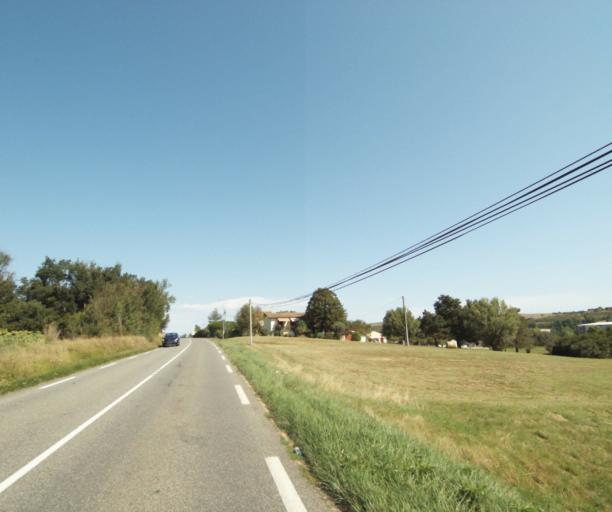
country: FR
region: Midi-Pyrenees
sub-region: Departement de l'Ariege
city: Lezat-sur-Leze
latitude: 43.2878
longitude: 1.3447
